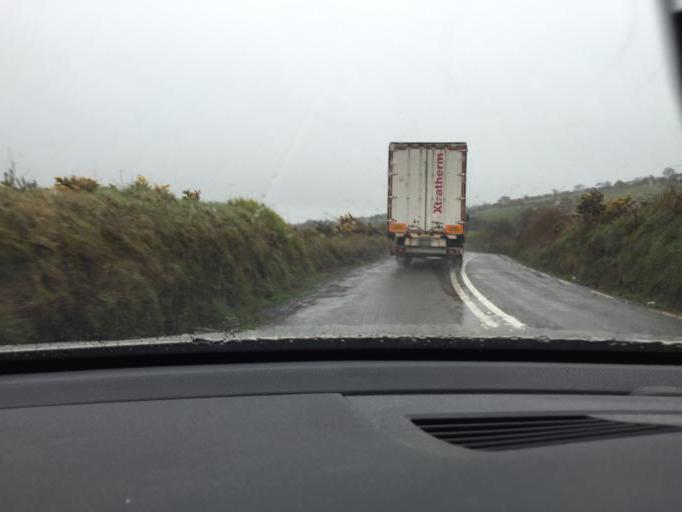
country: IE
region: Munster
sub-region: Ciarrai
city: Dingle
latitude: 52.1469
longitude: -10.1271
